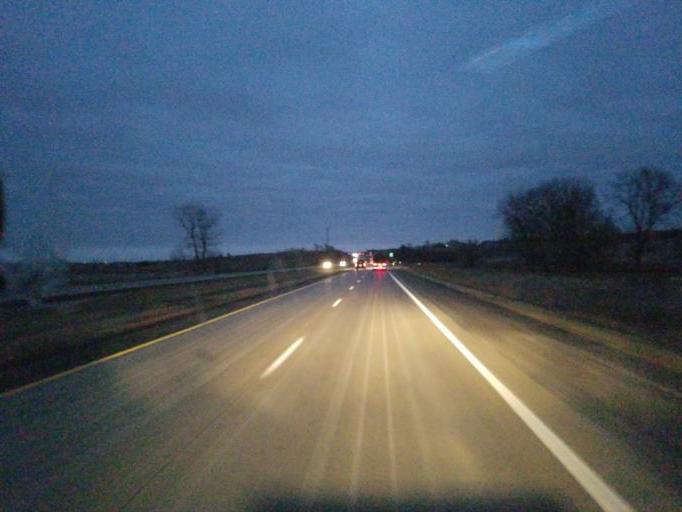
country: US
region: Iowa
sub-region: Cass County
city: Atlantic
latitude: 41.4964
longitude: -94.7933
